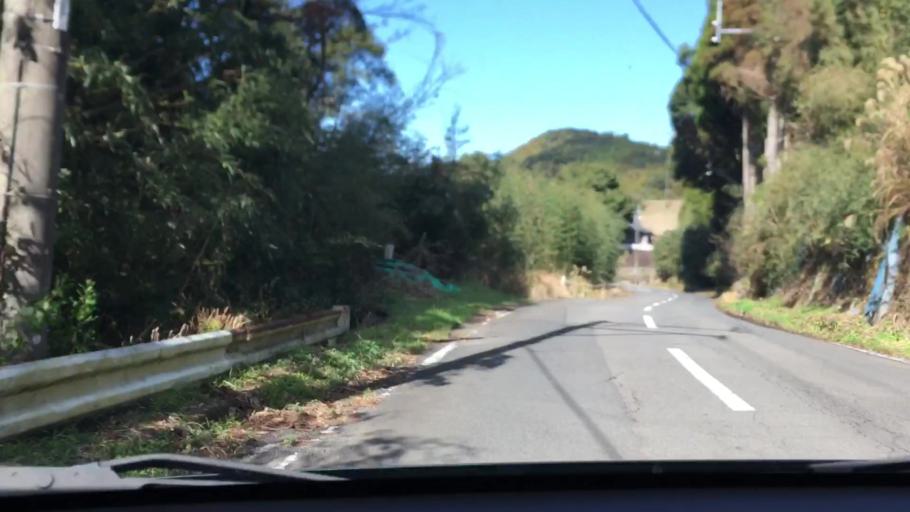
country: JP
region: Kagoshima
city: Ijuin
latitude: 31.7297
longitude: 130.4194
